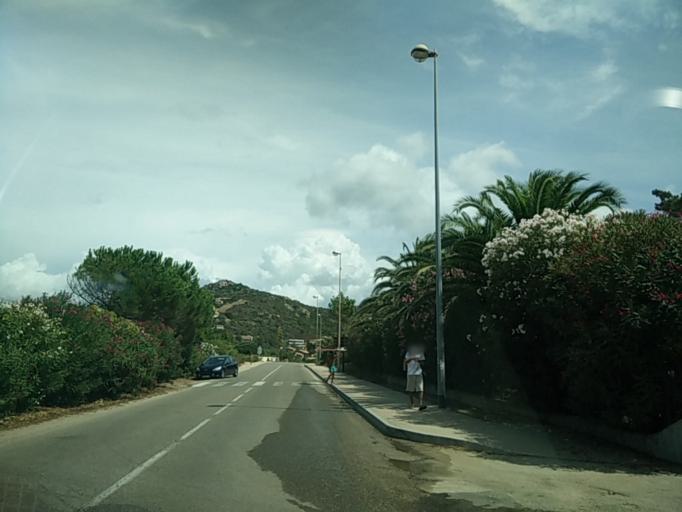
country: FR
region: Corsica
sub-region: Departement de la Corse-du-Sud
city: Pietrosella
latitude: 41.8285
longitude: 8.7837
